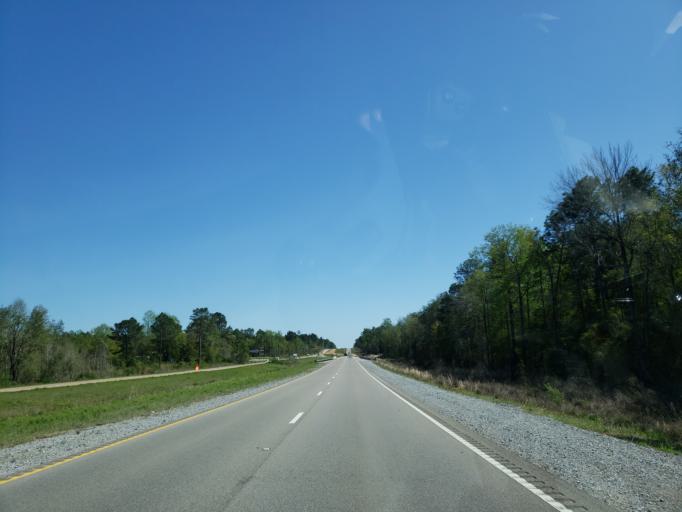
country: US
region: Mississippi
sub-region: Lamar County
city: Purvis
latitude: 31.1596
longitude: -89.2403
